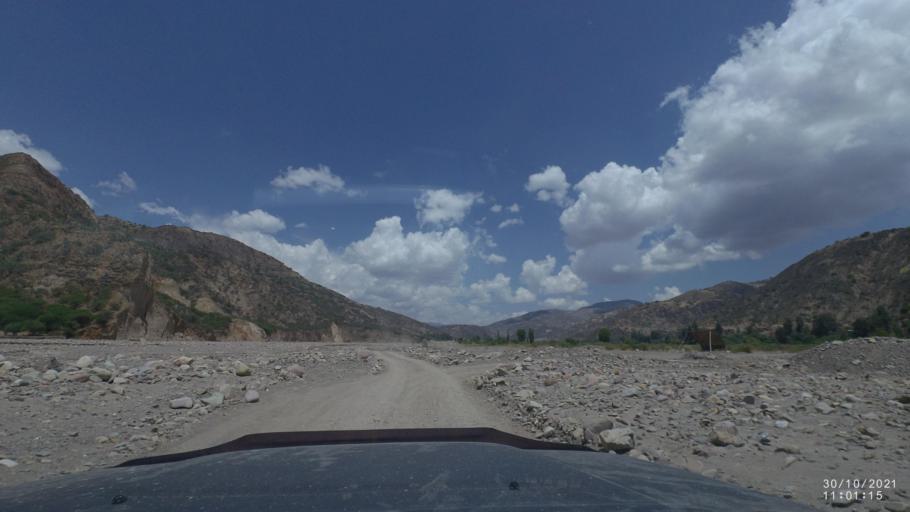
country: BO
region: Cochabamba
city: Sipe Sipe
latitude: -17.5347
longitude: -66.5200
